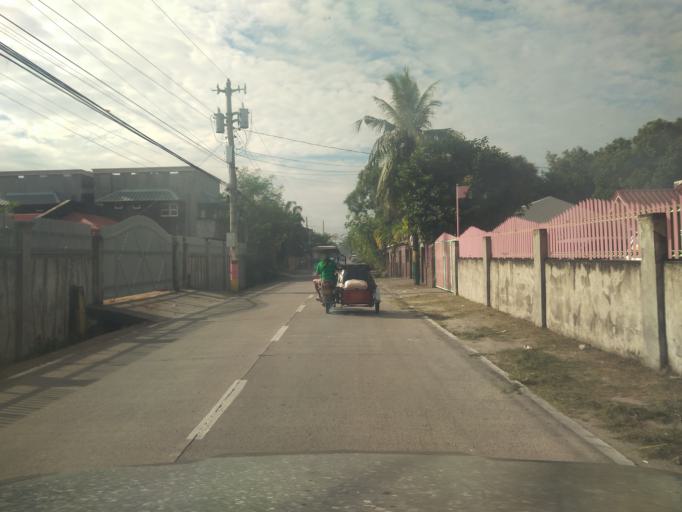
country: PH
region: Central Luzon
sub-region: Province of Pampanga
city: Sexmoan
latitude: 14.9456
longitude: 120.6228
